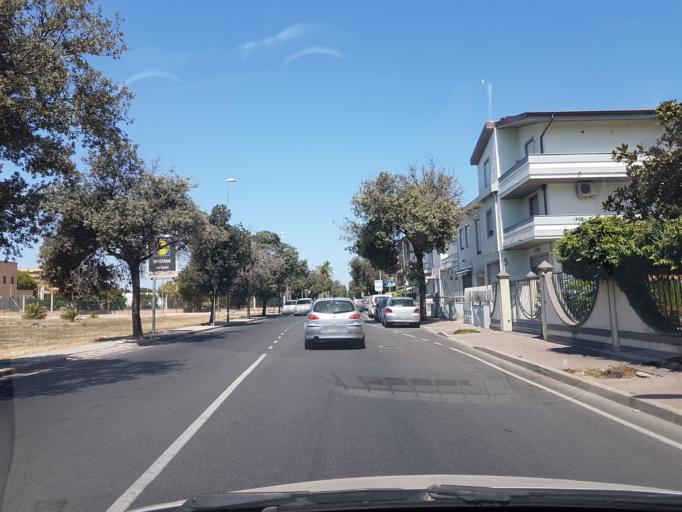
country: IT
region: Sardinia
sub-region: Provincia di Oristano
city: Oristano
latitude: 39.8931
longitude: 8.5981
